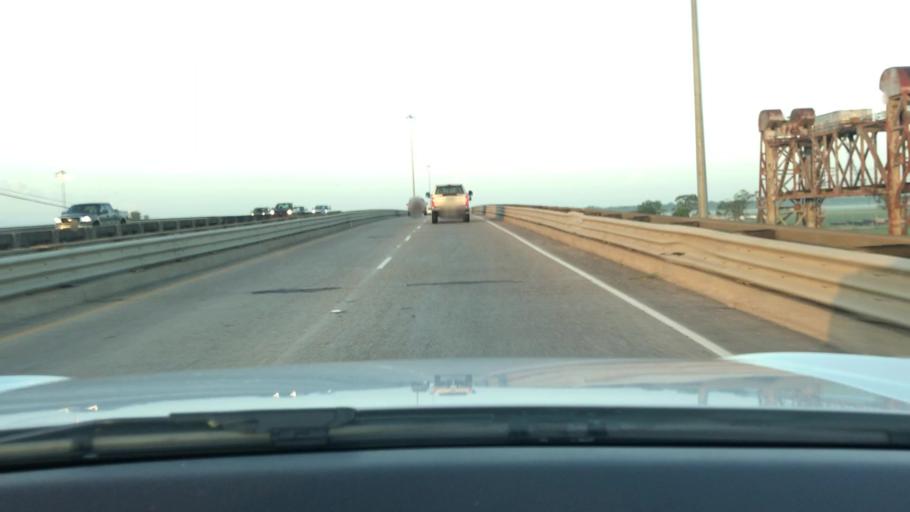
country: US
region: Louisiana
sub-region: West Baton Rouge Parish
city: Port Allen
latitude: 30.4335
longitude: -91.2106
